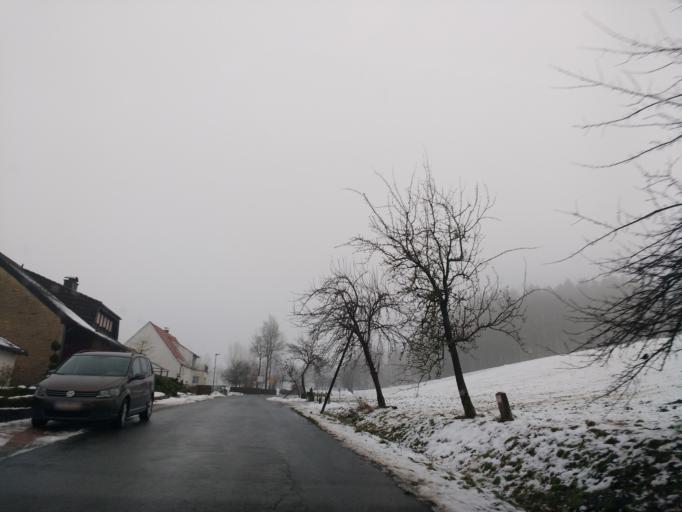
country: DE
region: North Rhine-Westphalia
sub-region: Regierungsbezirk Detmold
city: Altenbeken
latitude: 51.8018
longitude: 8.9453
